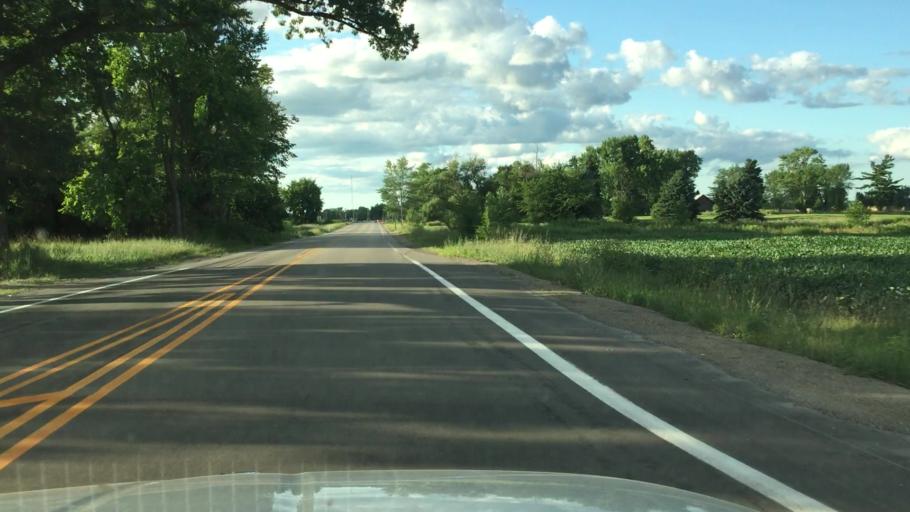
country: US
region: Michigan
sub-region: Saint Clair County
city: Capac
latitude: 42.9912
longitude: -82.9279
